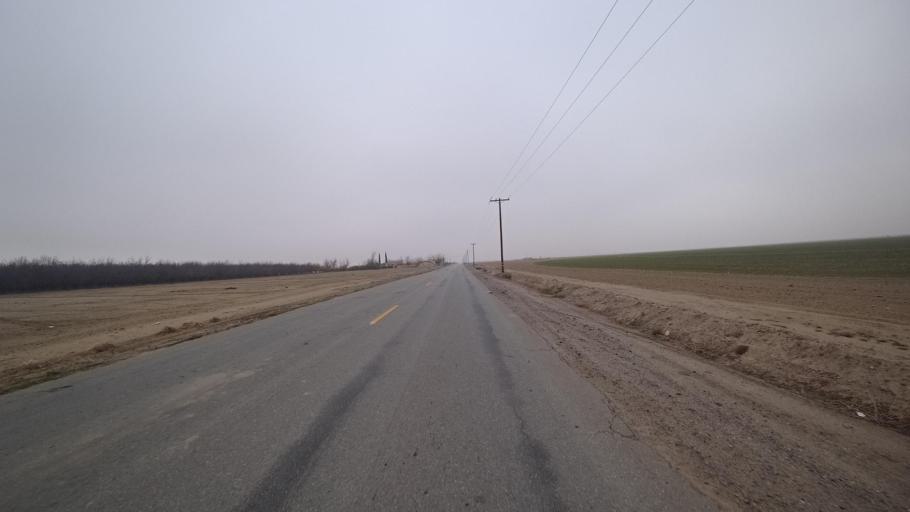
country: US
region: California
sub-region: Kern County
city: Greenfield
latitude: 35.0945
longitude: -119.1135
